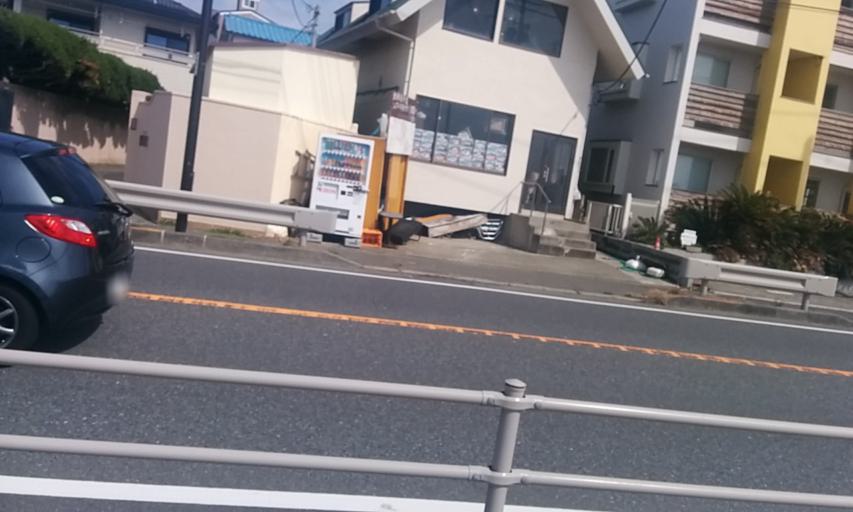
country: JP
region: Kanagawa
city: Kamakura
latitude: 35.3098
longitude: 139.5411
